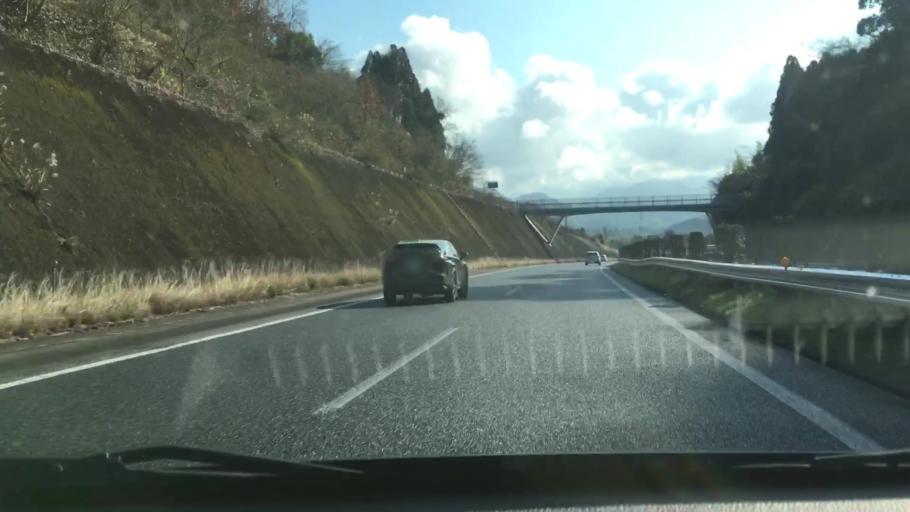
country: JP
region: Kumamoto
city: Matsubase
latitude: 32.5883
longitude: 130.7165
